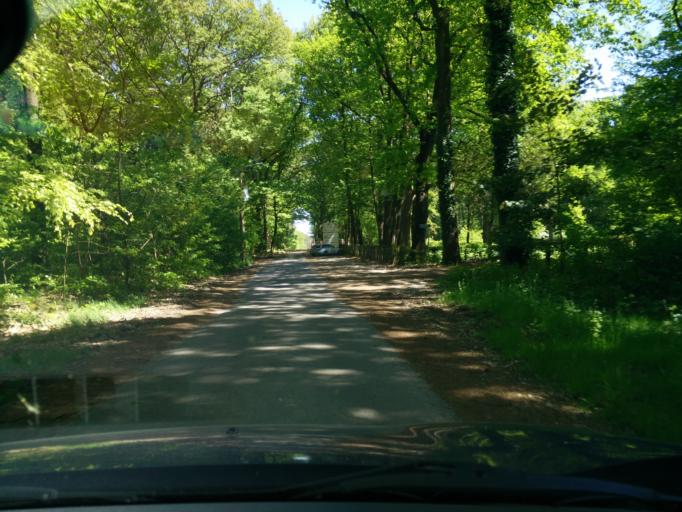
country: BE
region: Flanders
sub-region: Provincie Limburg
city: Maasmechelen
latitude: 51.0048
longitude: 5.6519
